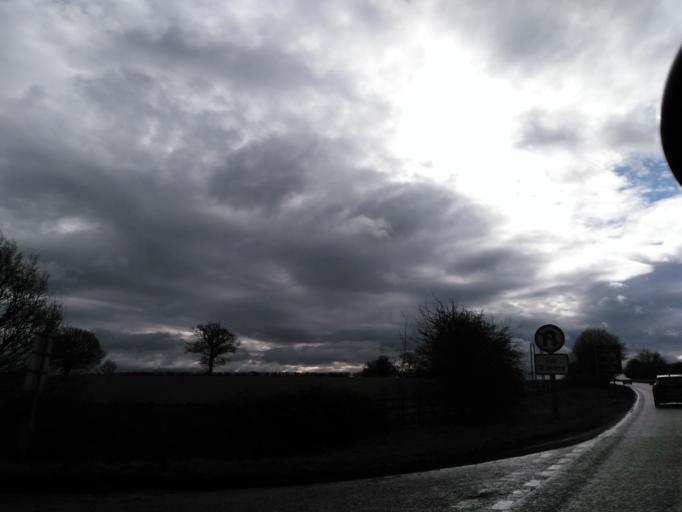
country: GB
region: England
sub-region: Wiltshire
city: Chippenham
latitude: 51.5106
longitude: -2.1243
